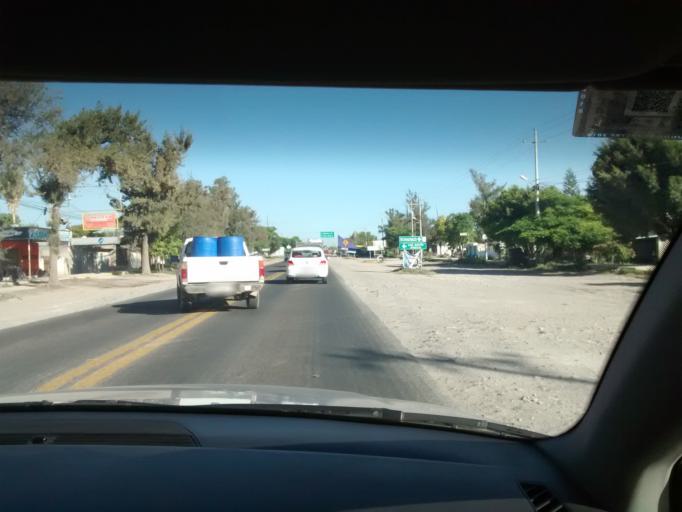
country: MX
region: Puebla
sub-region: Tehuacan
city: Magdalena Cuayucatepec
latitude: 18.5147
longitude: -97.4978
